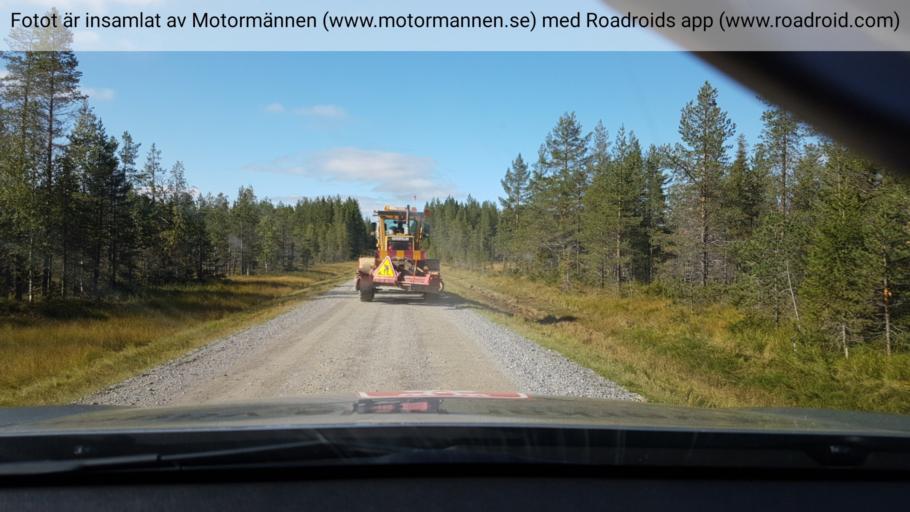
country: SE
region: Norrbotten
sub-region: Arvidsjaurs Kommun
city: Arvidsjaur
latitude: 65.2120
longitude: 19.1260
